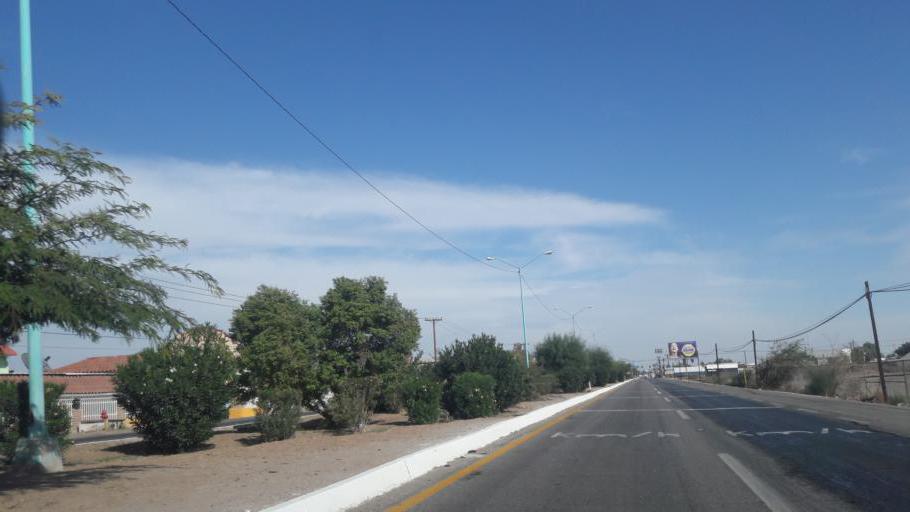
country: MX
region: Baja California
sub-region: Mexicali
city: Vinas del Sol
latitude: 32.6087
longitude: -115.5246
